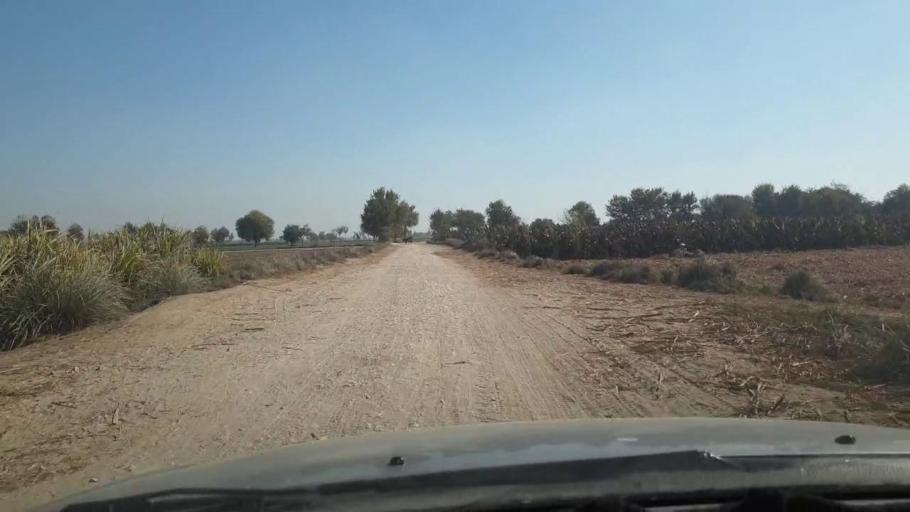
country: PK
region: Sindh
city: Ghotki
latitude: 28.0234
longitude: 69.2205
